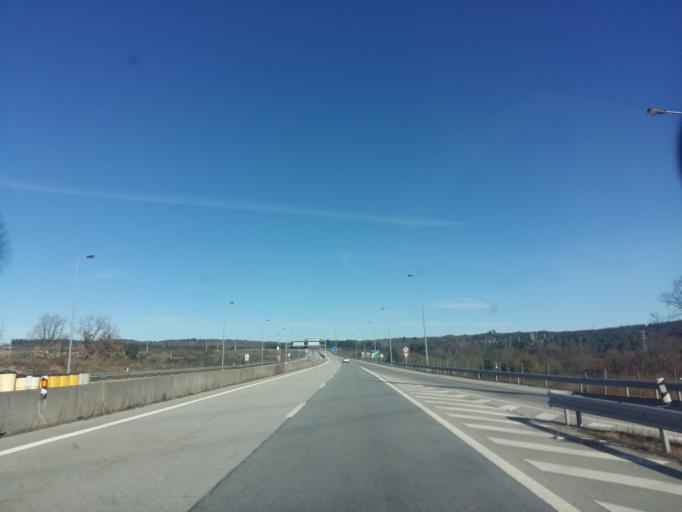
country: PT
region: Guarda
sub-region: Guarda
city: Sequeira
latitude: 40.5249
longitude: -7.2246
